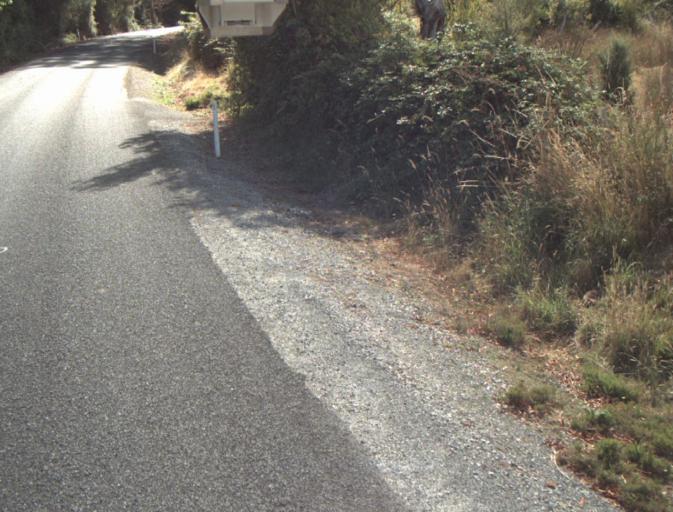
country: AU
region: Tasmania
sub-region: Launceston
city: Mayfield
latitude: -41.2585
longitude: 147.1810
